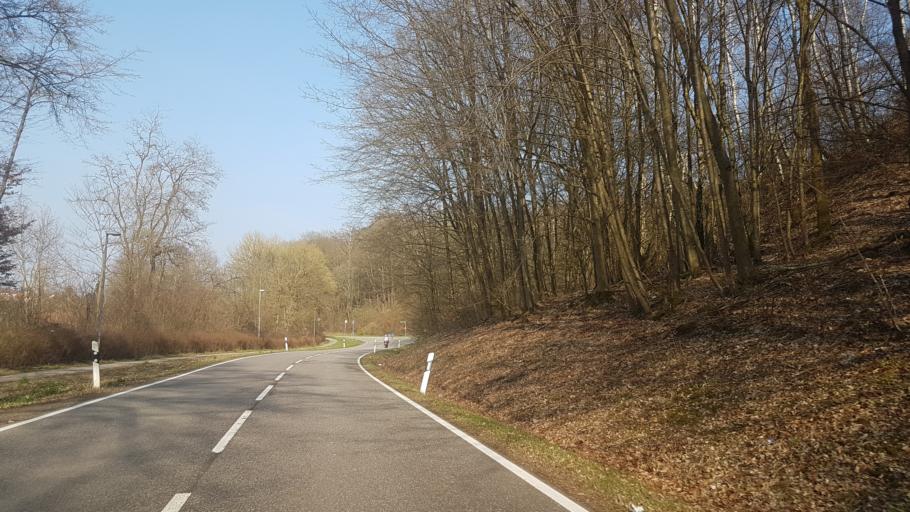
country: DE
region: Saarland
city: Sulzbach
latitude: 49.3035
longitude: 7.0765
